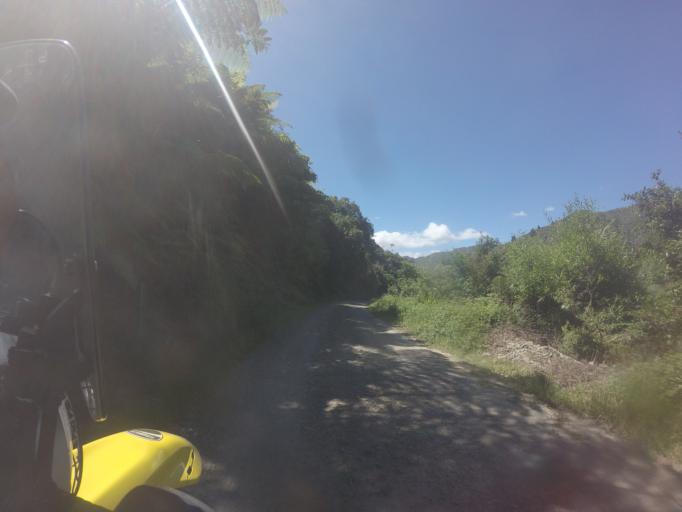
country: NZ
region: Bay of Plenty
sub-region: Opotiki District
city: Opotiki
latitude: -38.3042
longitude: 177.3306
